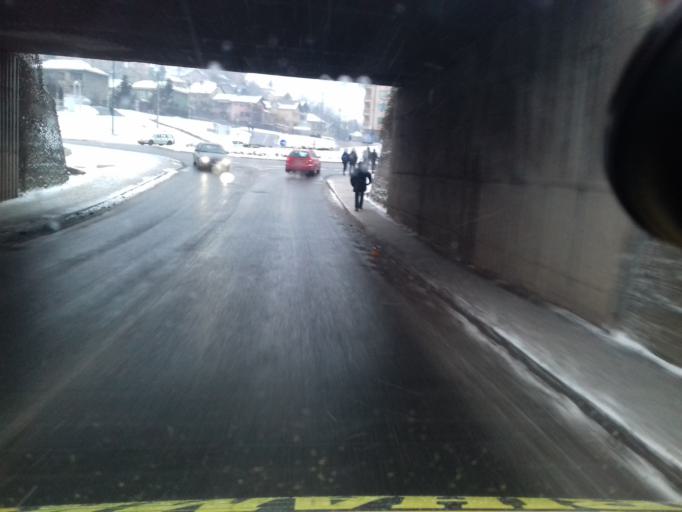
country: BA
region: Federation of Bosnia and Herzegovina
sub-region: Kanton Sarajevo
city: Sarajevo
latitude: 43.8533
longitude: 18.3652
